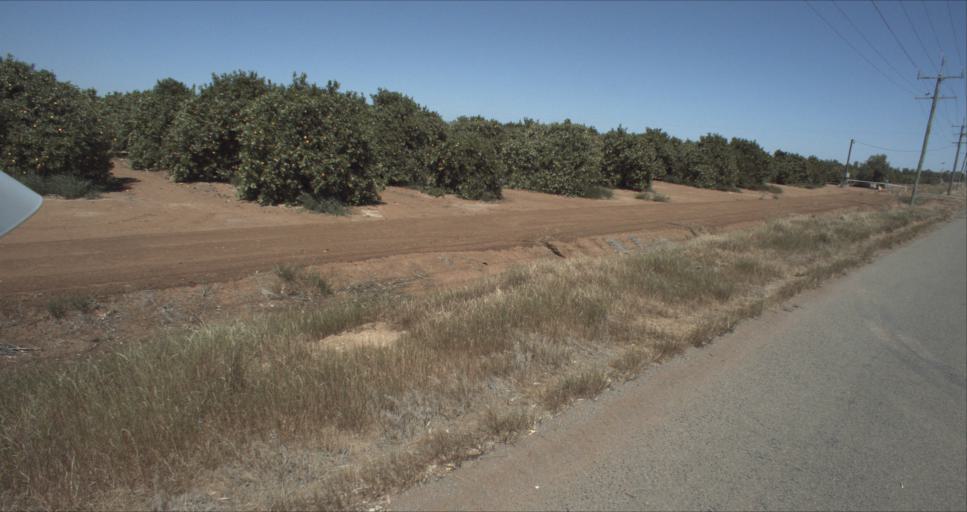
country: AU
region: New South Wales
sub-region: Leeton
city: Leeton
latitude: -34.4964
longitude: 146.4212
